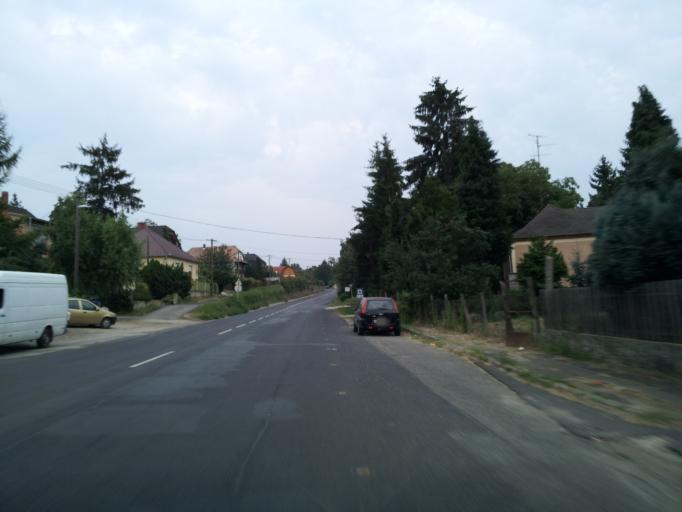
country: HU
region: Vas
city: Sarvar
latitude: 47.2444
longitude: 16.9658
